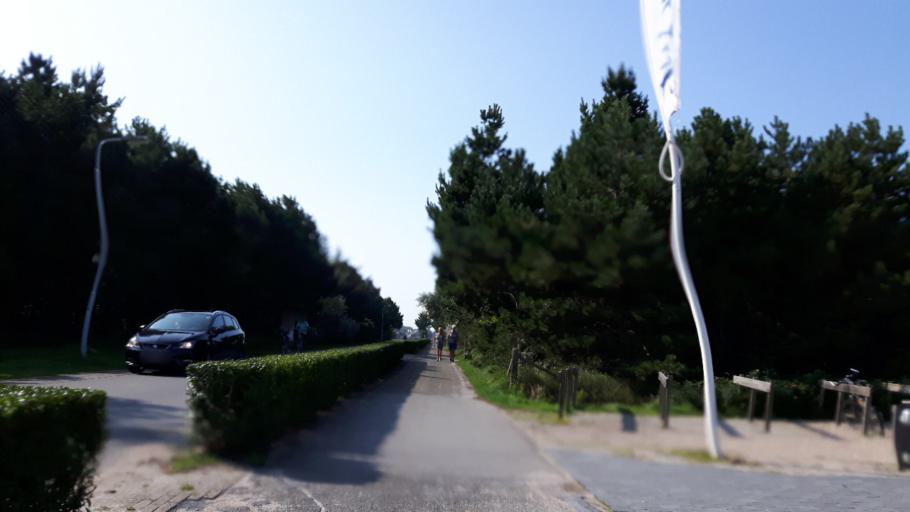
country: NL
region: Friesland
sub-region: Gemeente Ameland
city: Nes
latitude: 53.4555
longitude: 5.8039
